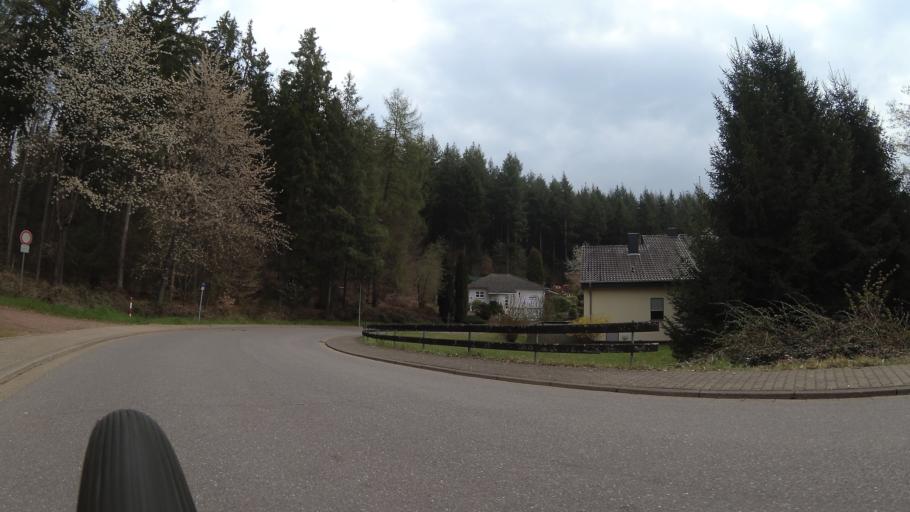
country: DE
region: Saarland
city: Mettlach
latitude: 49.4776
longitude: 6.6147
